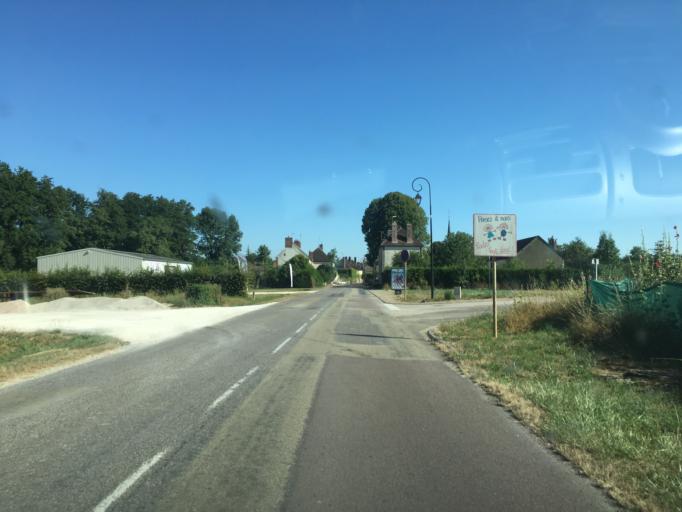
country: FR
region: Bourgogne
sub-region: Departement de l'Yonne
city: Aillant-sur-Tholon
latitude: 47.9084
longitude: 3.3579
